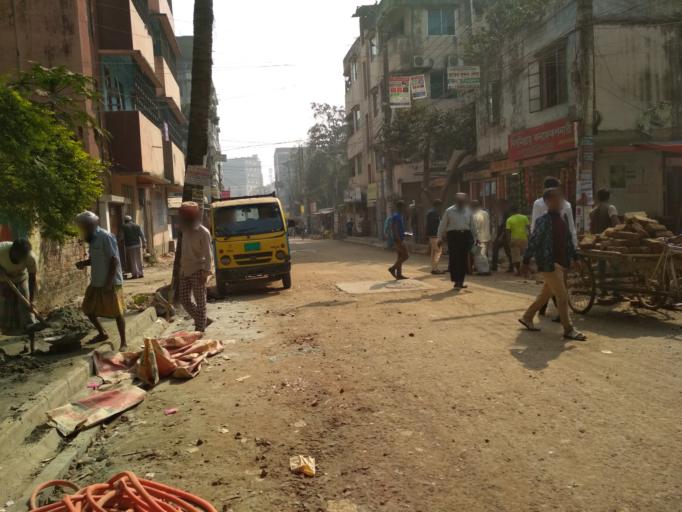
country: BD
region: Dhaka
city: Azimpur
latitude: 23.8092
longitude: 90.3712
